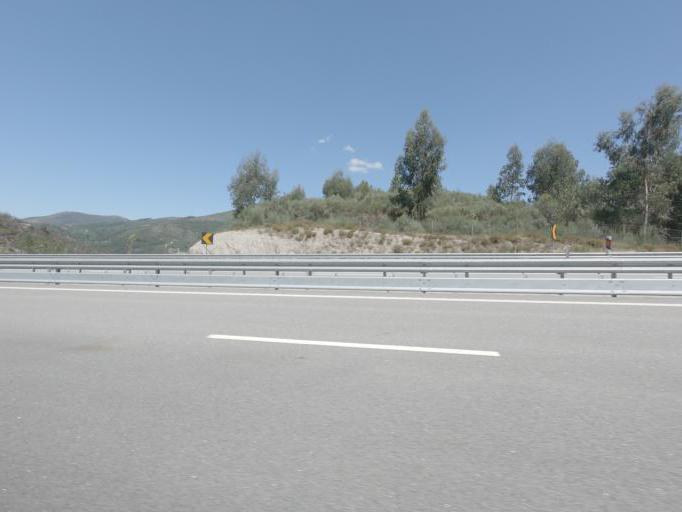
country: PT
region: Porto
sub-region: Amarante
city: Amarante
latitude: 41.2561
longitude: -7.9956
